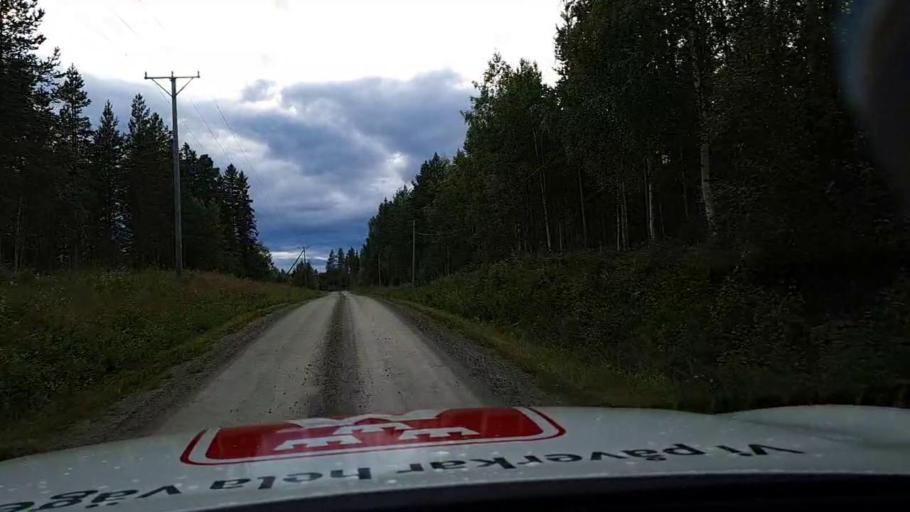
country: SE
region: Jaemtland
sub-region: Bergs Kommun
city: Hoverberg
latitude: 62.8922
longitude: 14.5597
